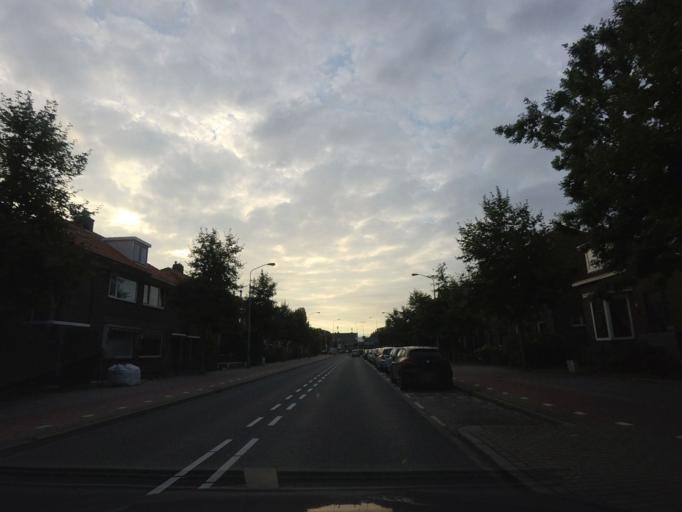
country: NL
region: North Holland
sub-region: Gemeente Zaanstad
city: Zaanstad
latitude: 52.4857
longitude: 4.8046
